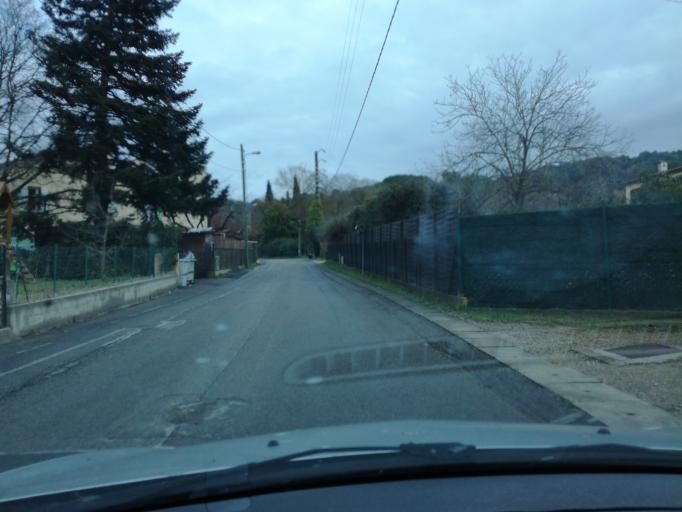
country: FR
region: Provence-Alpes-Cote d'Azur
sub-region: Departement des Alpes-Maritimes
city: Mouans-Sartoux
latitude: 43.6056
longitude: 6.9748
